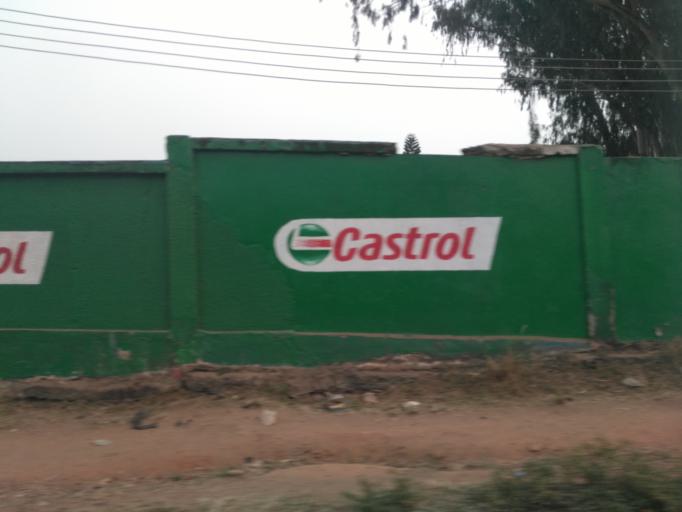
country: GH
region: Ashanti
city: Kumasi
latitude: 6.6802
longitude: -1.6125
